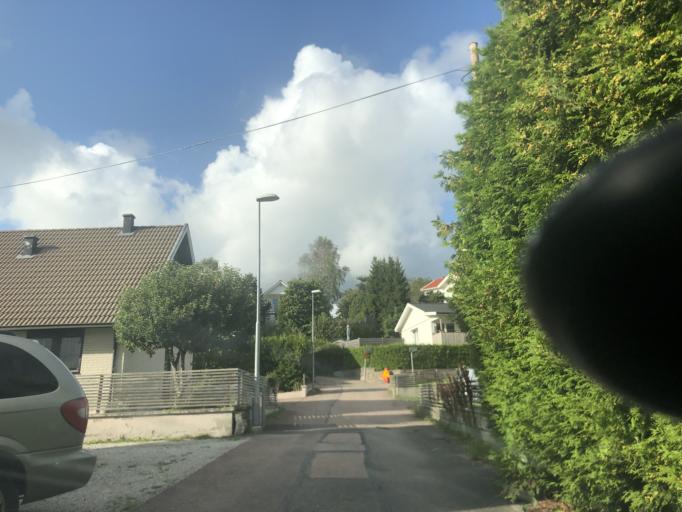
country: SE
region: Vaestra Goetaland
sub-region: Goteborg
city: Goeteborg
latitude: 57.7451
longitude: 11.9551
